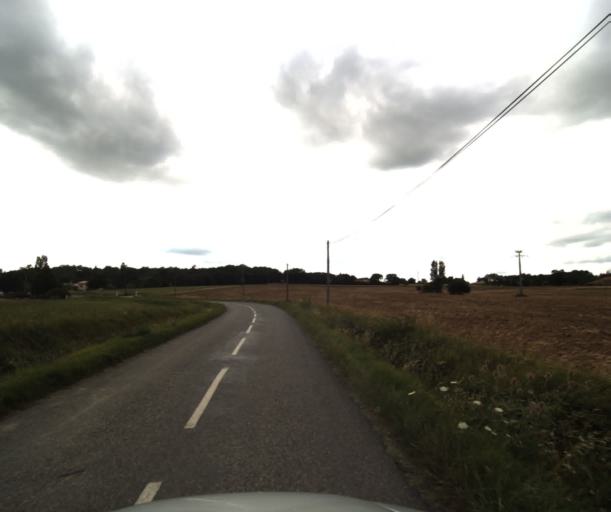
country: FR
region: Midi-Pyrenees
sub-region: Departement de la Haute-Garonne
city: Eaunes
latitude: 43.4206
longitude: 1.3480
